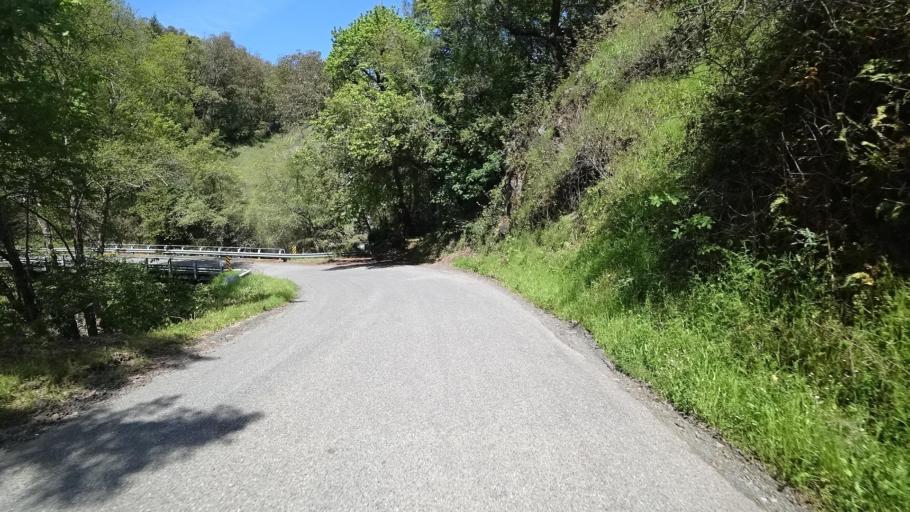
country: US
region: California
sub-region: Humboldt County
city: Redway
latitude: 40.2732
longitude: -123.6250
